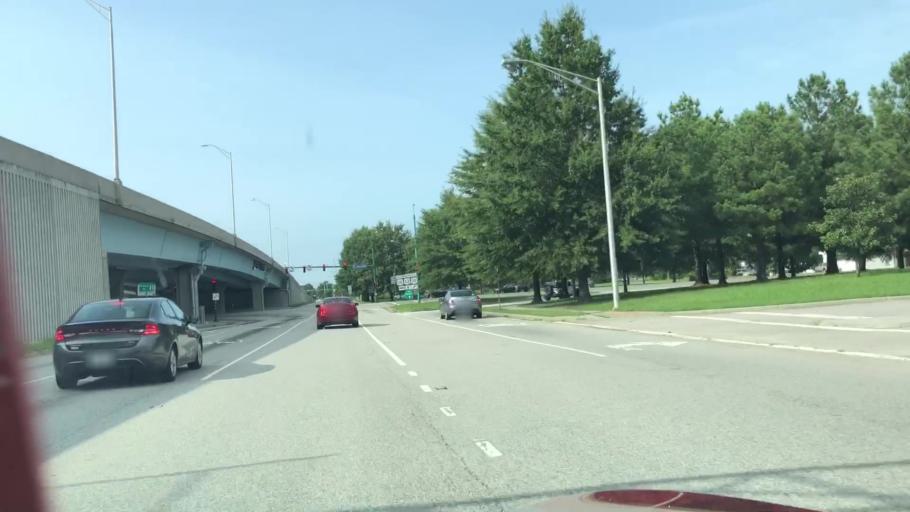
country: US
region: Virginia
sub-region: City of Chesapeake
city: Chesapeake
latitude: 36.8548
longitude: -76.2097
